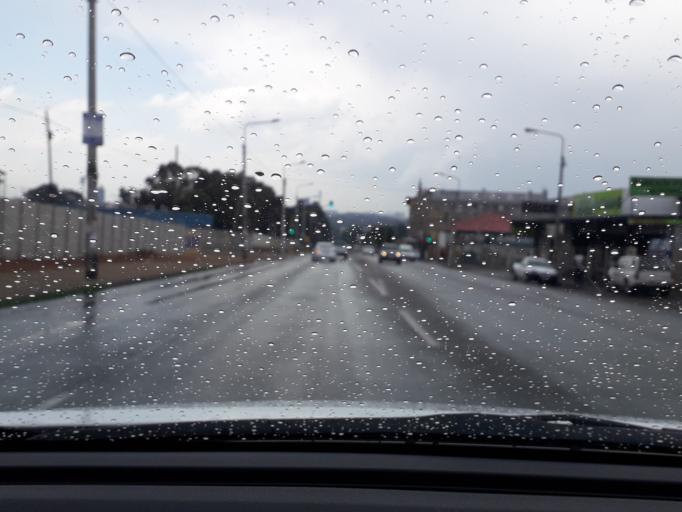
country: ZA
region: Gauteng
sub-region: City of Johannesburg Metropolitan Municipality
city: Johannesburg
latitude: -26.2407
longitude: 28.0532
